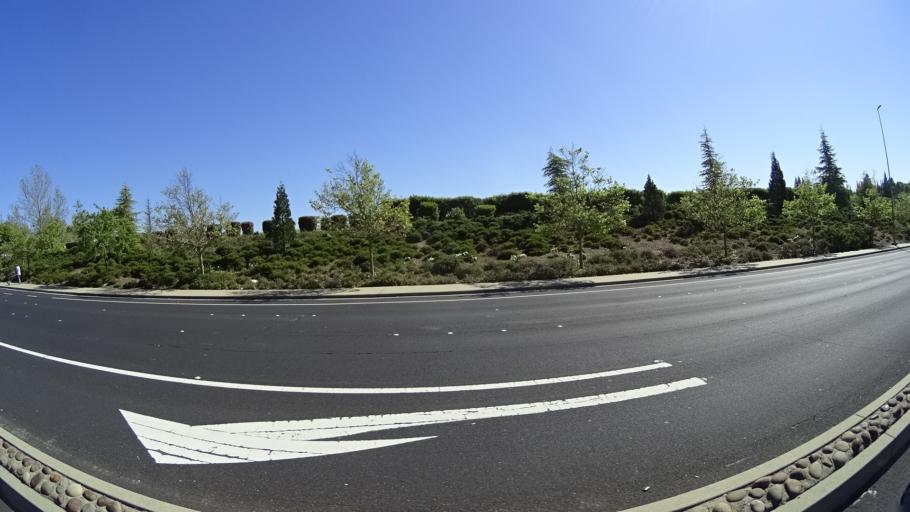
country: US
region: California
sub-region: Placer County
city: Rocklin
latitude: 38.7875
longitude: -121.2677
